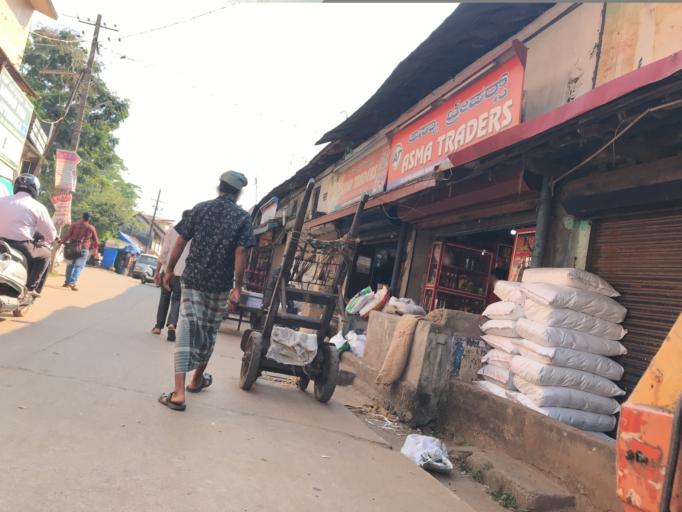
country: IN
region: Karnataka
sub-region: Dakshina Kannada
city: Mangalore
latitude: 12.8640
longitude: 74.8328
